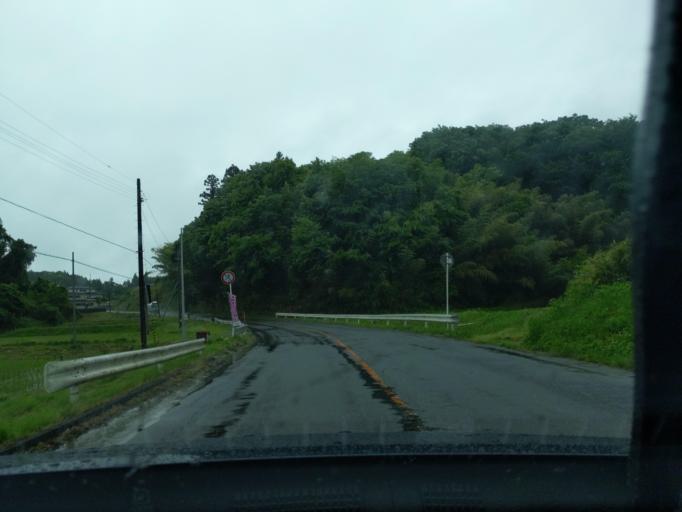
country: JP
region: Fukushima
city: Nihommatsu
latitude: 37.5256
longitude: 140.4862
